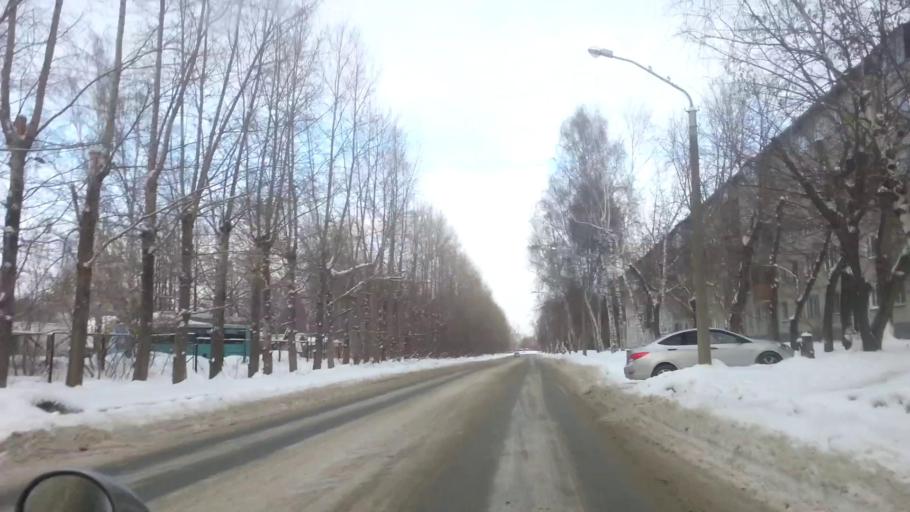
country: RU
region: Altai Krai
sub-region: Gorod Barnaulskiy
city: Barnaul
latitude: 53.3666
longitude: 83.6932
